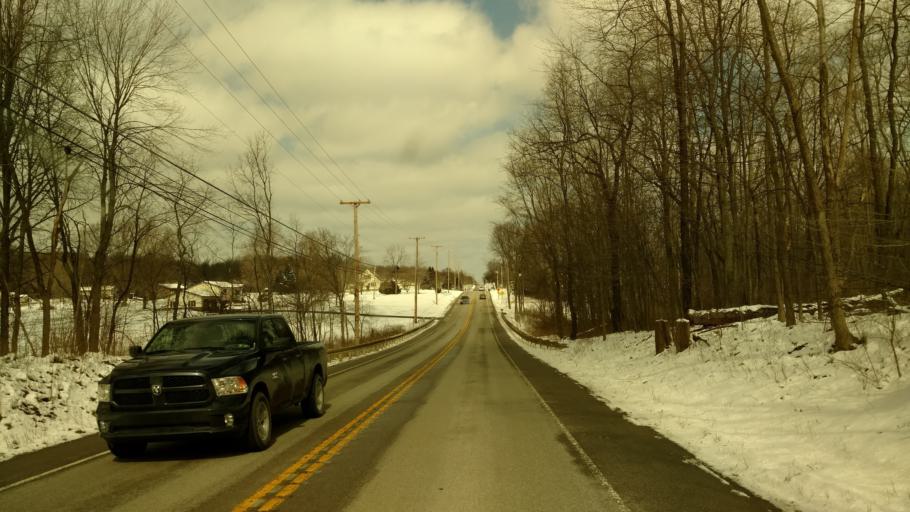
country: US
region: Pennsylvania
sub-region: Mercer County
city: Mercer
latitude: 41.3358
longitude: -80.2281
